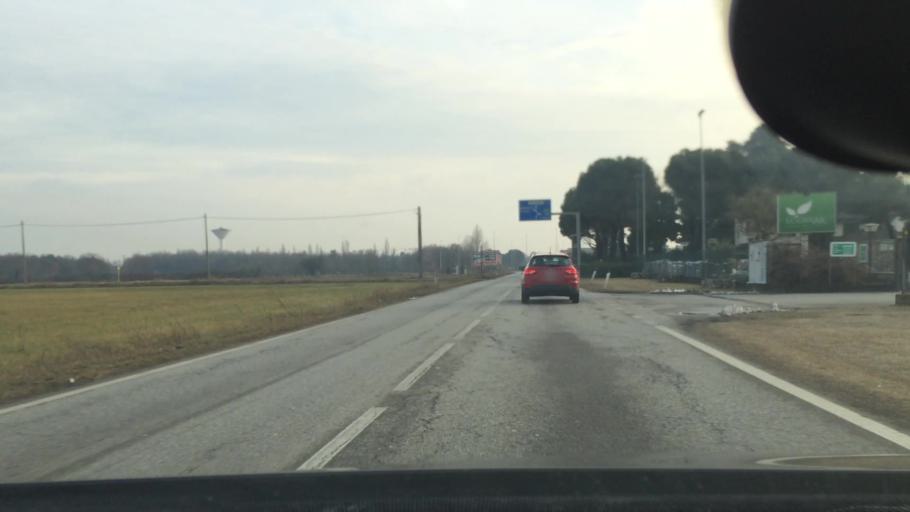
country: IT
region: Lombardy
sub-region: Provincia di Varese
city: Origgio
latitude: 45.5860
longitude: 9.0245
